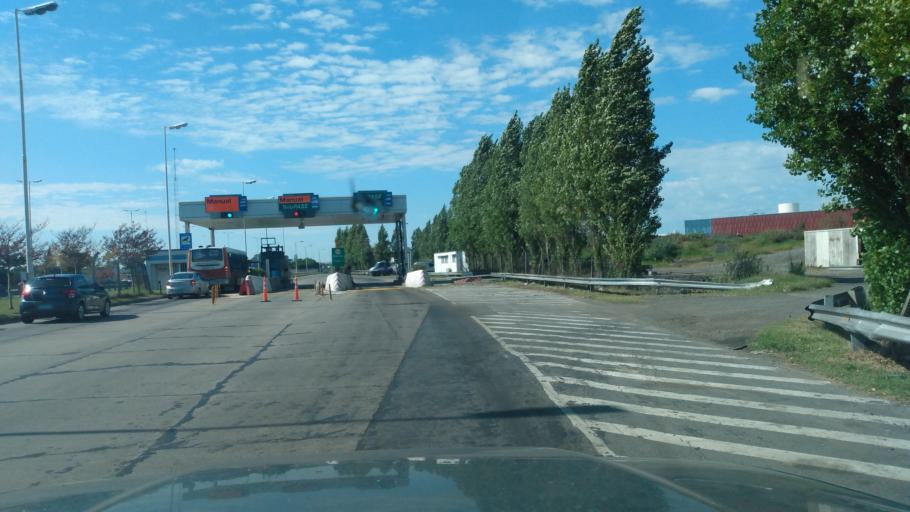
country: AR
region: Buenos Aires
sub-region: Partido de Merlo
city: Merlo
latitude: -34.6285
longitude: -58.7301
